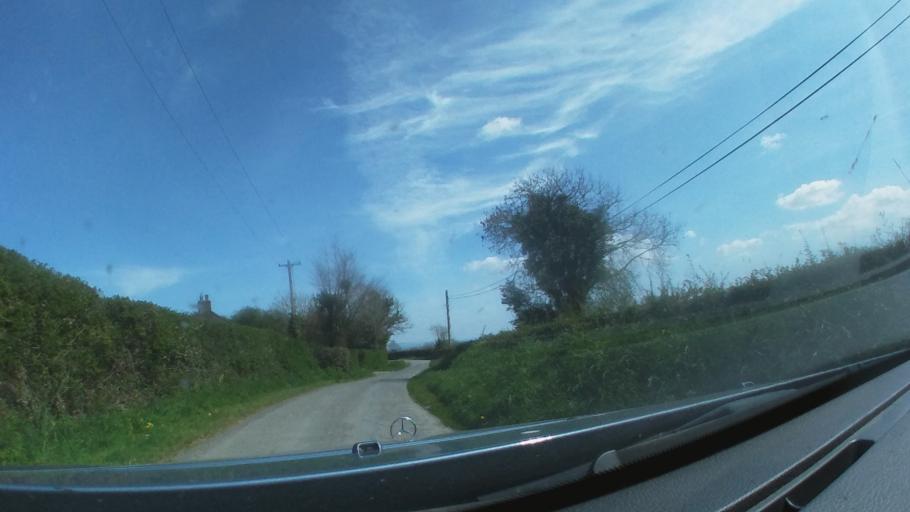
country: IE
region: Leinster
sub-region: Kilkenny
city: Callan
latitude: 52.6238
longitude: -7.4710
